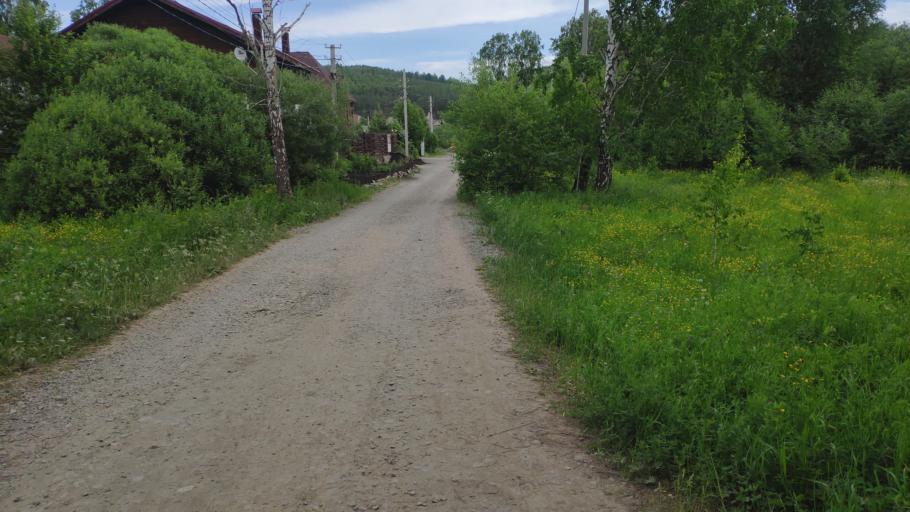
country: RU
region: Bashkortostan
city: Abzakovo
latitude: 53.8127
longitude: 58.6356
